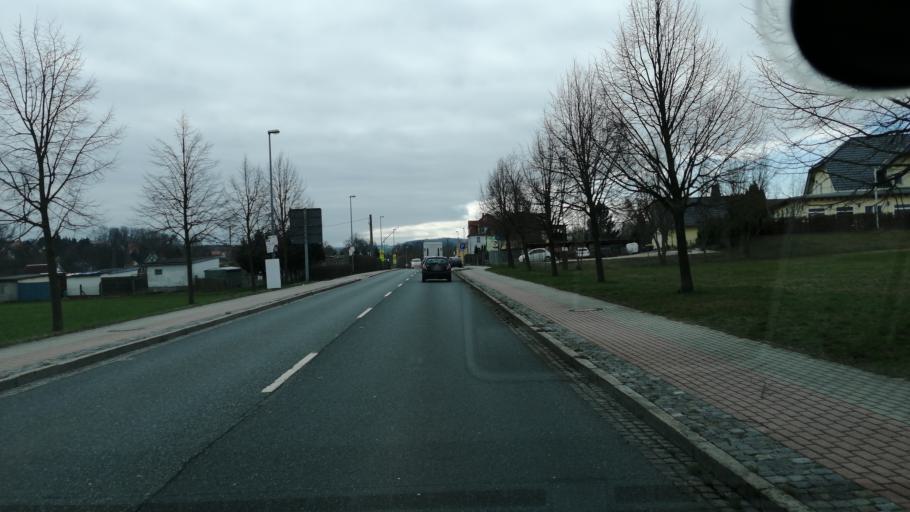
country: DE
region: Saxony
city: Lobau
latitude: 51.0861
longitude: 14.6714
